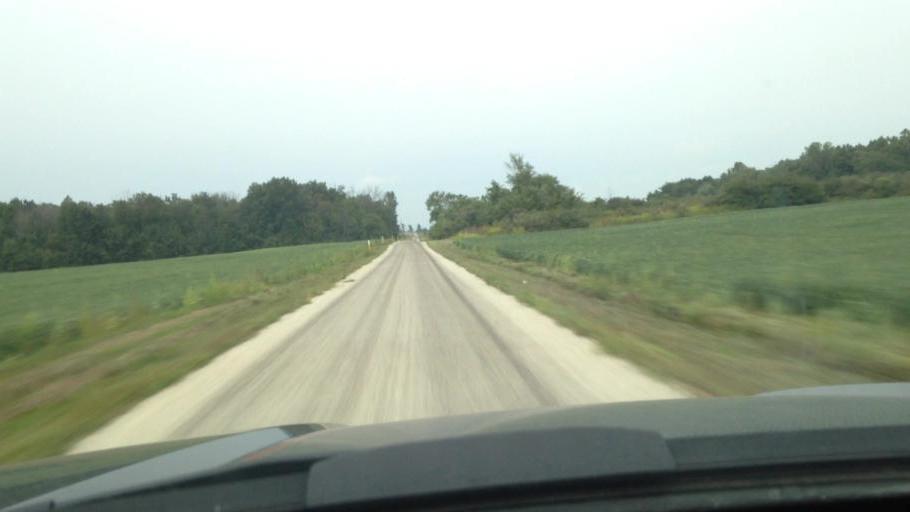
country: US
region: Indiana
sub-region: Randolph County
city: Union City
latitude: 40.2178
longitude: -84.8615
